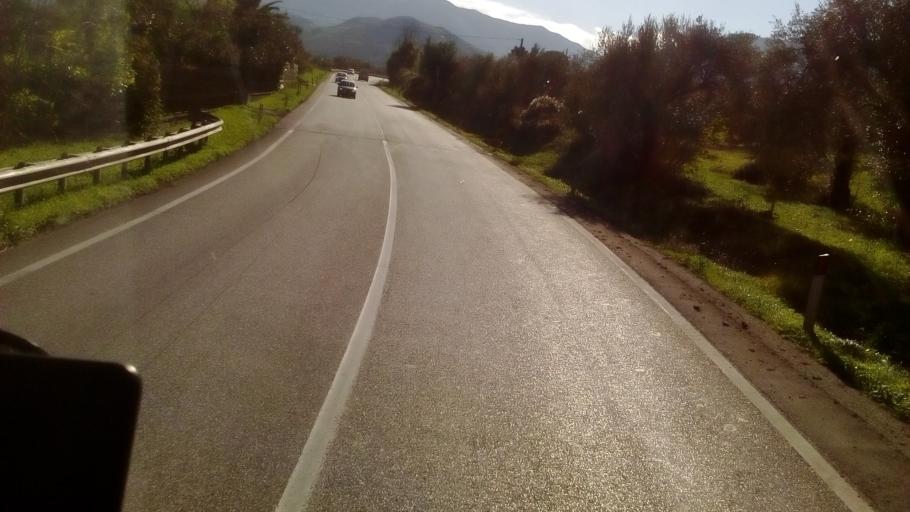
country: IT
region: Molise
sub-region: Provincia di Isernia
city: Venafro
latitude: 41.4762
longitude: 14.0302
